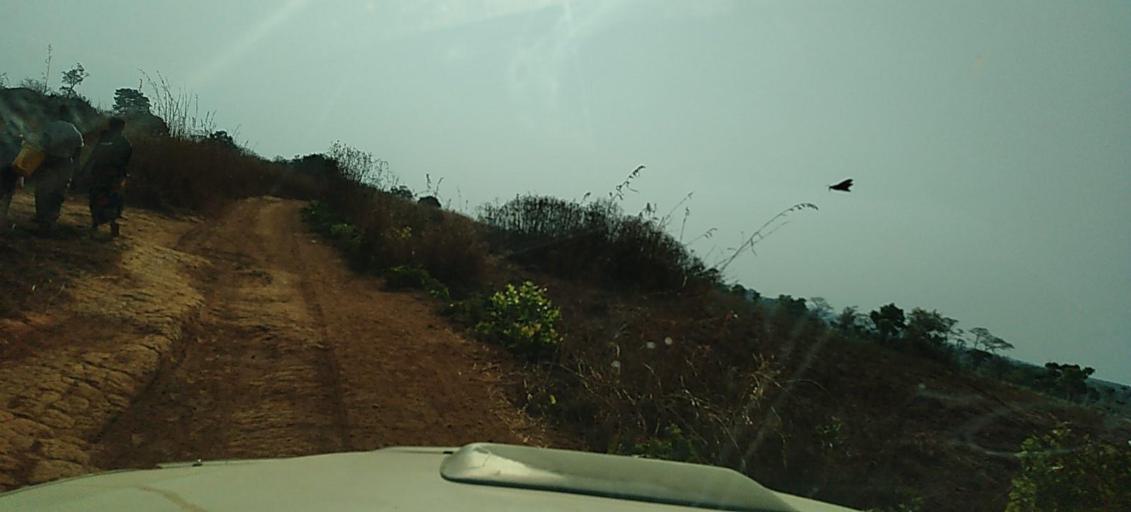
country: ZM
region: North-Western
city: Kasempa
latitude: -13.1830
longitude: 25.9483
